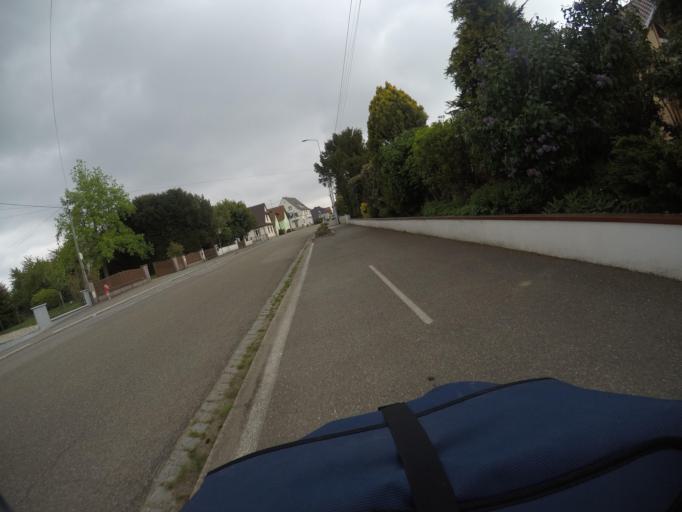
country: DE
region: Baden-Wuerttemberg
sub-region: Karlsruhe Region
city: Greffern
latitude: 48.7909
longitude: 7.9903
